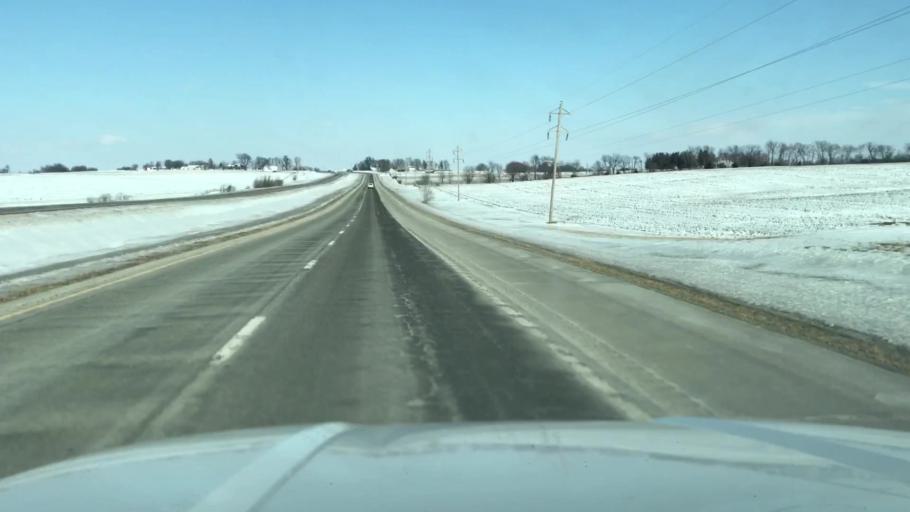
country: US
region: Missouri
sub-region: Nodaway County
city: Maryville
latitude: 40.2614
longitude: -94.8667
